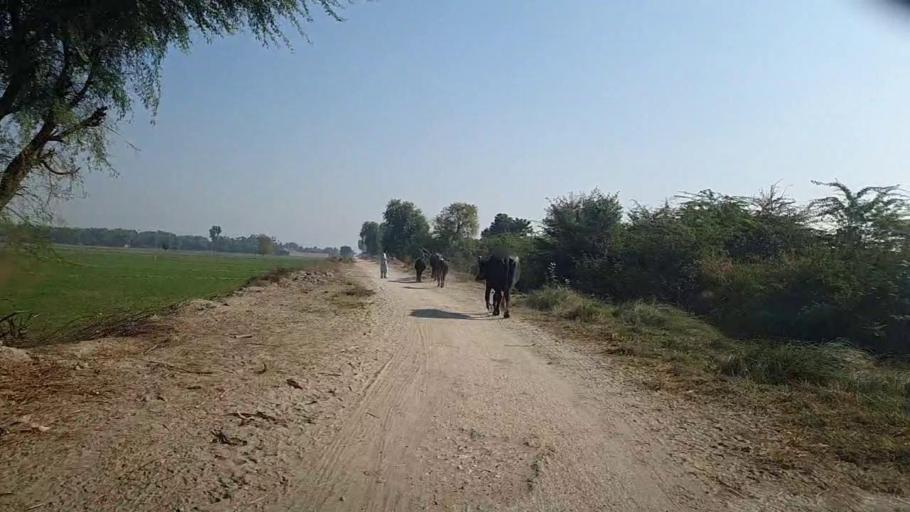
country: PK
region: Sindh
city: Darya Khan Marri
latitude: 26.7095
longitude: 68.3229
